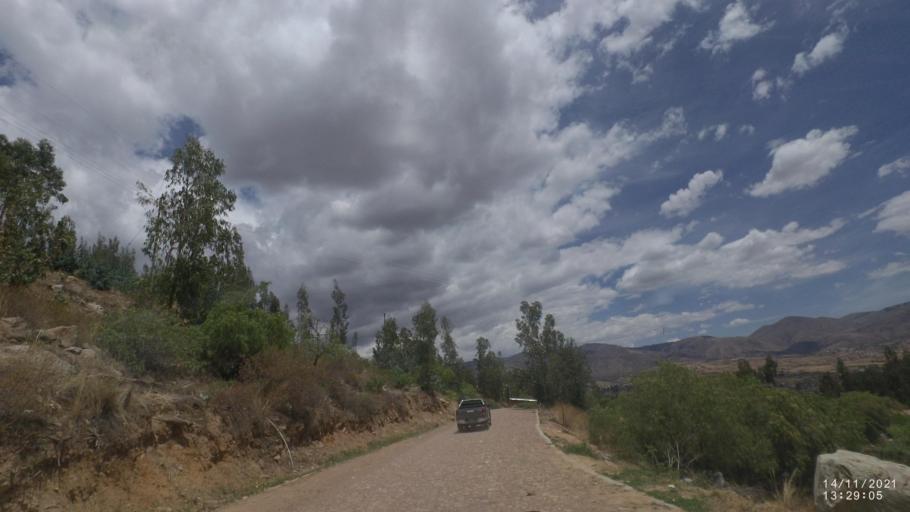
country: BO
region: Cochabamba
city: Colomi
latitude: -17.3877
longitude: -65.9848
